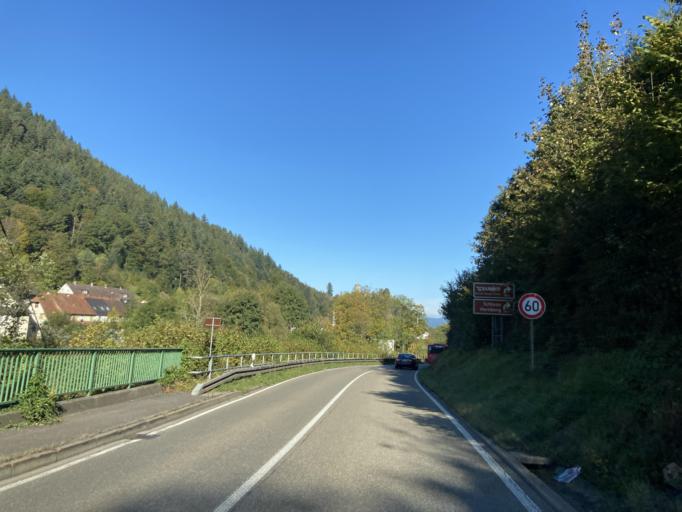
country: DE
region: Baden-Wuerttemberg
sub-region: Freiburg Region
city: Hornberg
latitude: 48.2021
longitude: 8.2350
